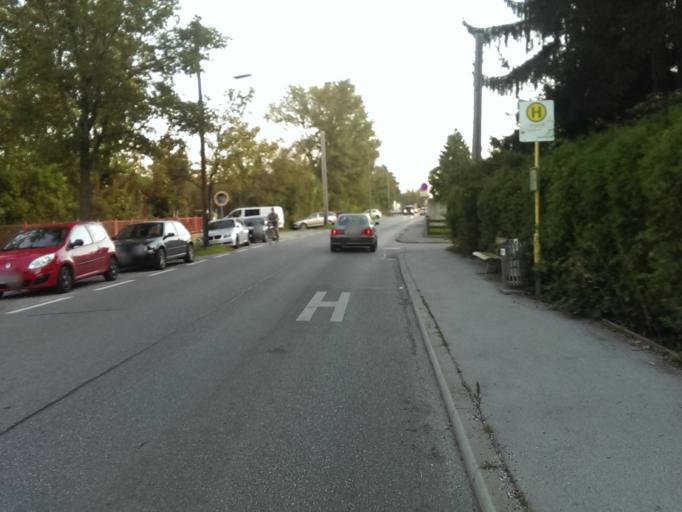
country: AT
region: Styria
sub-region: Graz Stadt
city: Goesting
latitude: 47.0903
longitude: 15.4026
